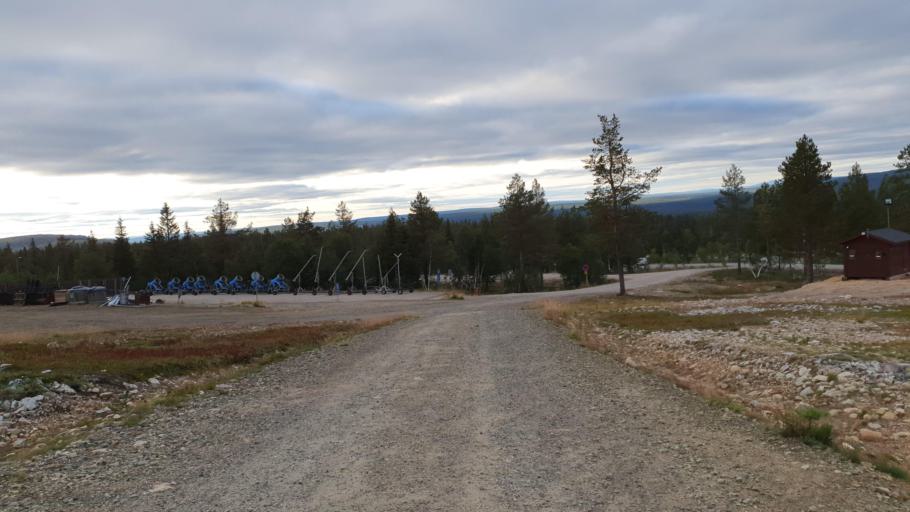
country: FI
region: Lapland
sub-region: Tunturi-Lappi
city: Kolari
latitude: 67.5801
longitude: 24.2053
